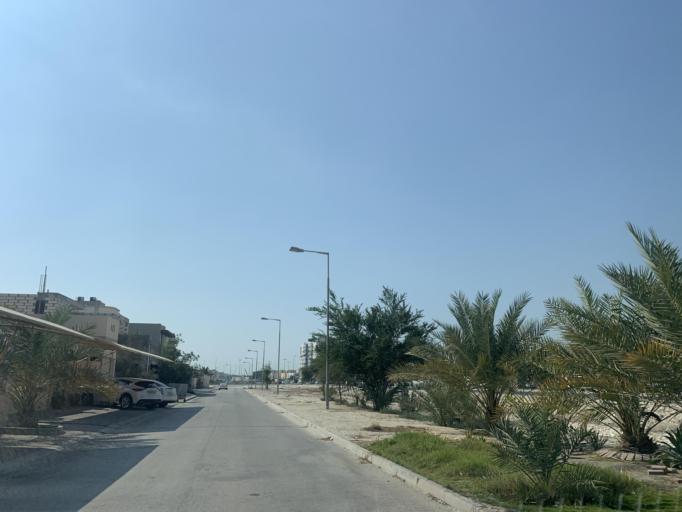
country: BH
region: Central Governorate
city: Madinat Hamad
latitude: 26.1149
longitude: 50.4959
